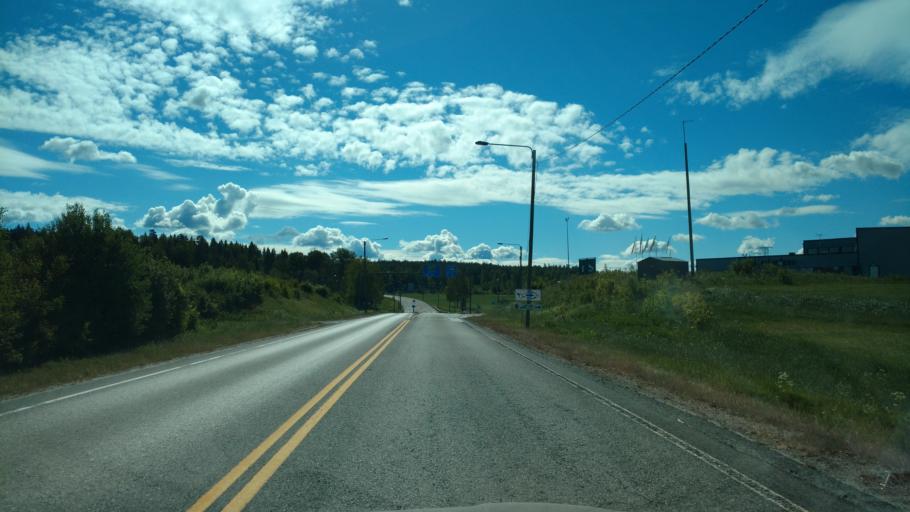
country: FI
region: Varsinais-Suomi
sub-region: Salo
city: Muurla
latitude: 60.3750
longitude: 23.3108
